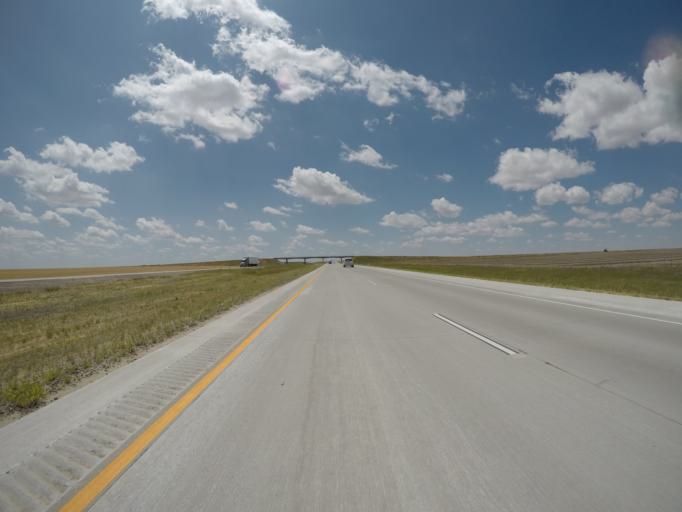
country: US
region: Colorado
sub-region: Kit Carson County
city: Burlington
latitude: 39.2943
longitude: -102.7773
